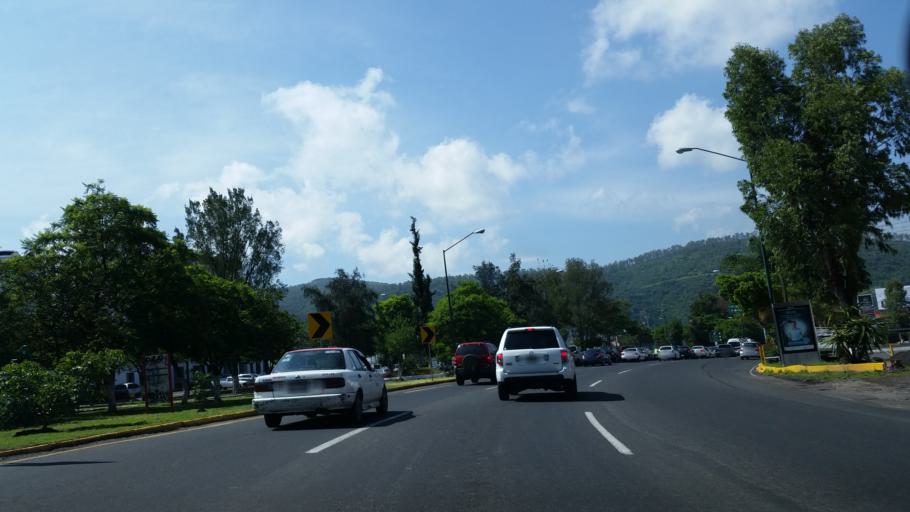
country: MX
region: Michoacan
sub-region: Morelia
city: Puerto de Buenavista (Lazaro Cardenas)
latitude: 19.6959
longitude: -101.1496
